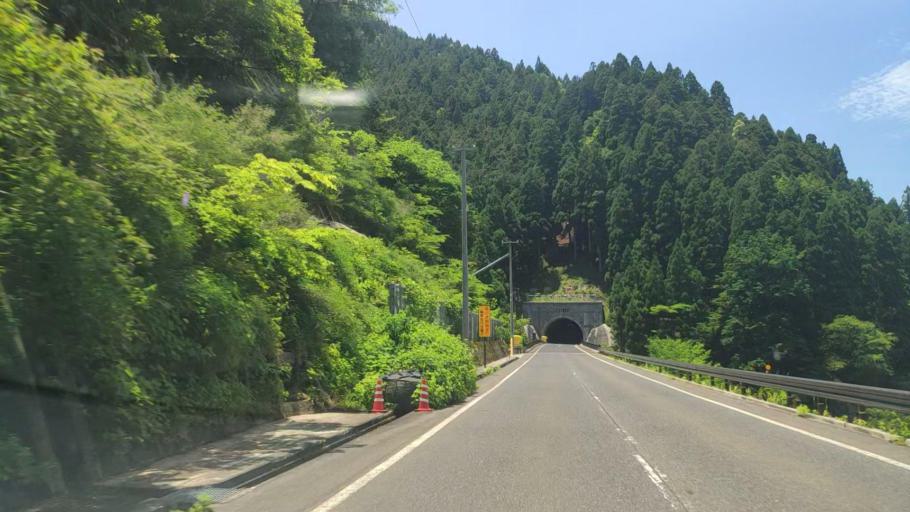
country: JP
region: Tottori
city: Tottori
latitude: 35.3477
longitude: 134.4621
